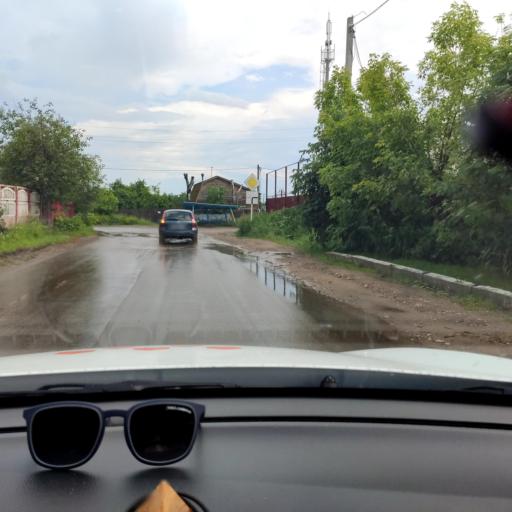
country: RU
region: Tatarstan
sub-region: Zelenodol'skiy Rayon
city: Vasil'yevo
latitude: 55.8290
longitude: 48.7058
